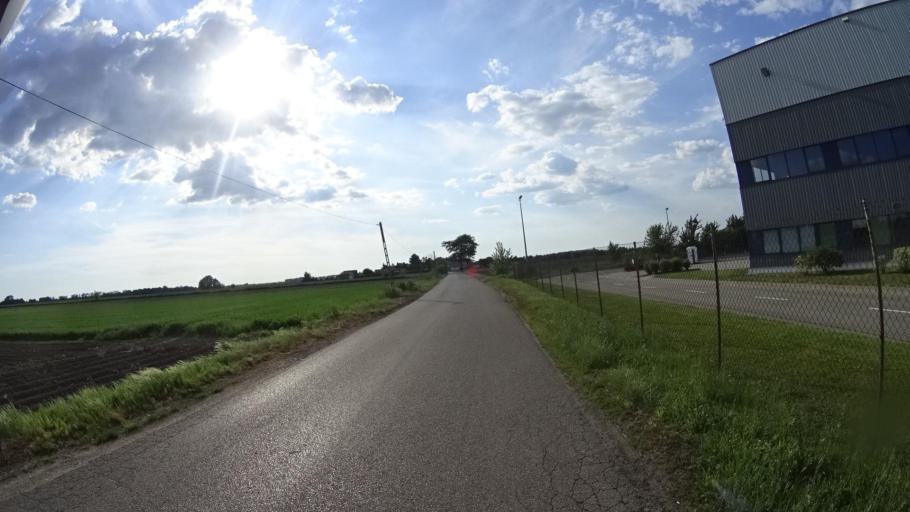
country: PL
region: Masovian Voivodeship
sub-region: Powiat warszawski zachodni
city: Ozarow Mazowiecki
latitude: 52.2017
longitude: 20.7654
